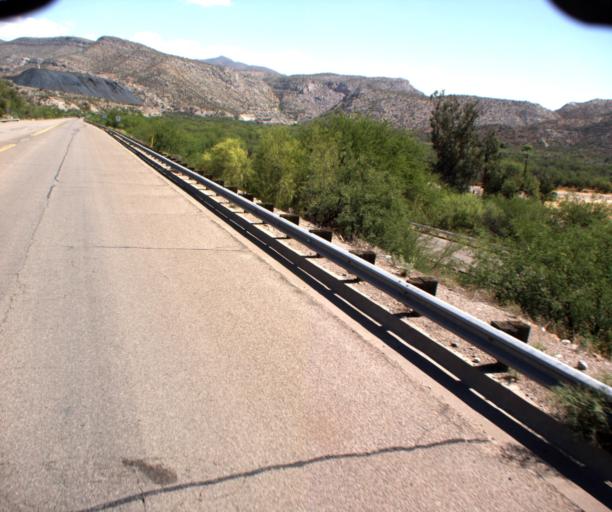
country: US
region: Arizona
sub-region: Pinal County
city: Kearny
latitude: 32.9890
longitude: -110.7696
